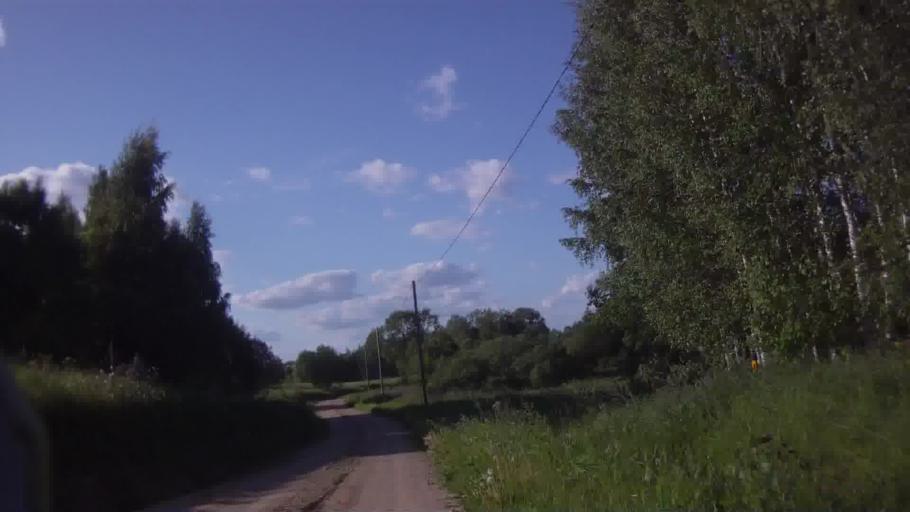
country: LV
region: Dagda
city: Dagda
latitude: 56.2771
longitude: 27.4686
